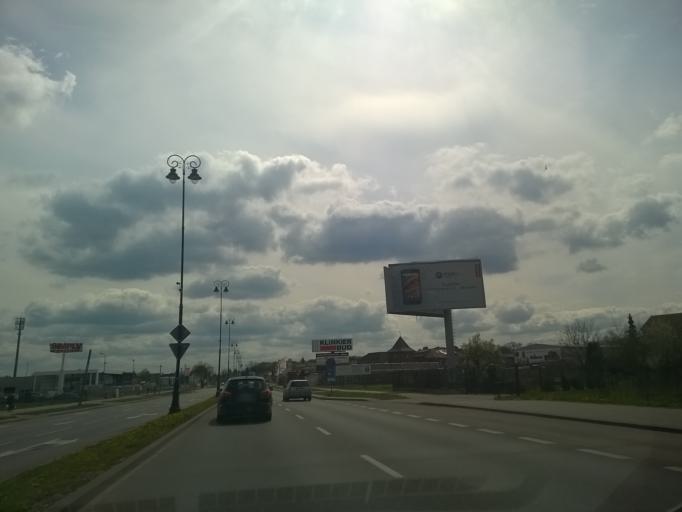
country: PL
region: Masovian Voivodeship
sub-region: Powiat piaseczynski
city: Konstancin-Jeziorna
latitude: 52.1085
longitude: 21.1130
